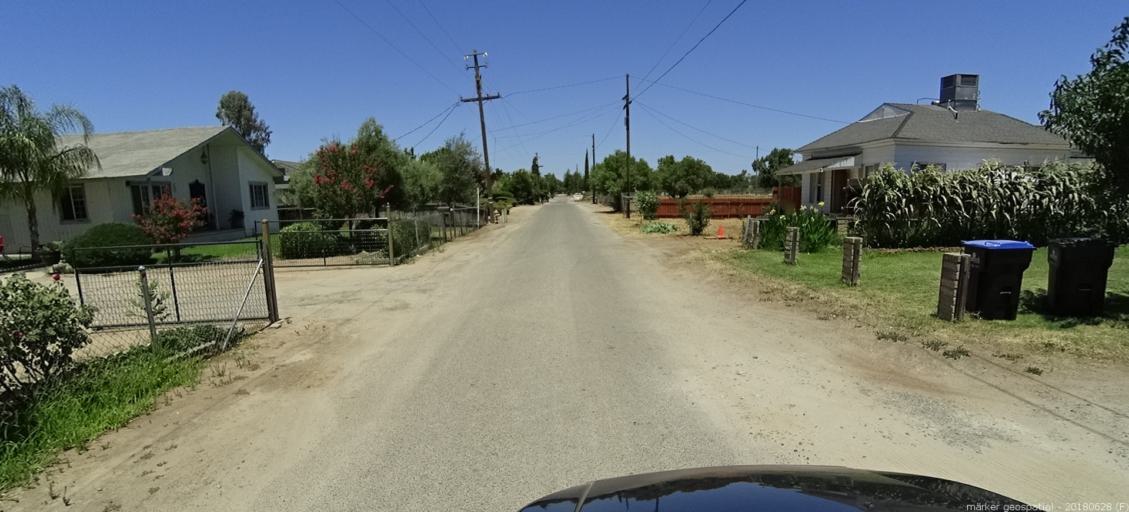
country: US
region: California
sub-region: Madera County
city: Parksdale
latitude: 36.9414
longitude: -120.0297
